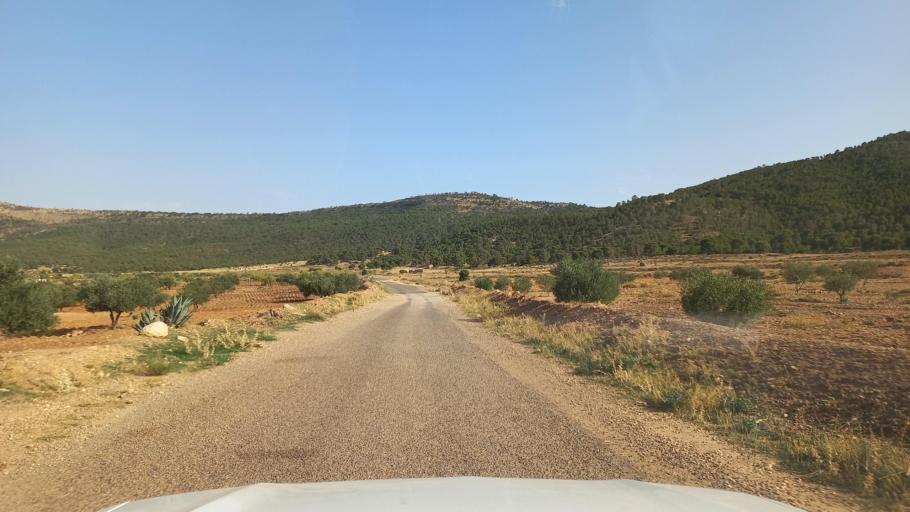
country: TN
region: Al Qasrayn
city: Kasserine
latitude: 35.3380
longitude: 8.8363
